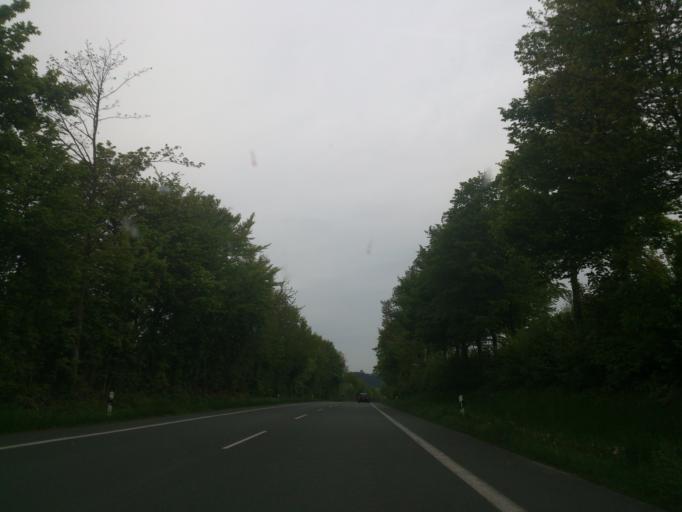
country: DE
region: North Rhine-Westphalia
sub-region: Regierungsbezirk Detmold
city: Altenbeken
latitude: 51.7173
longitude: 8.9422
